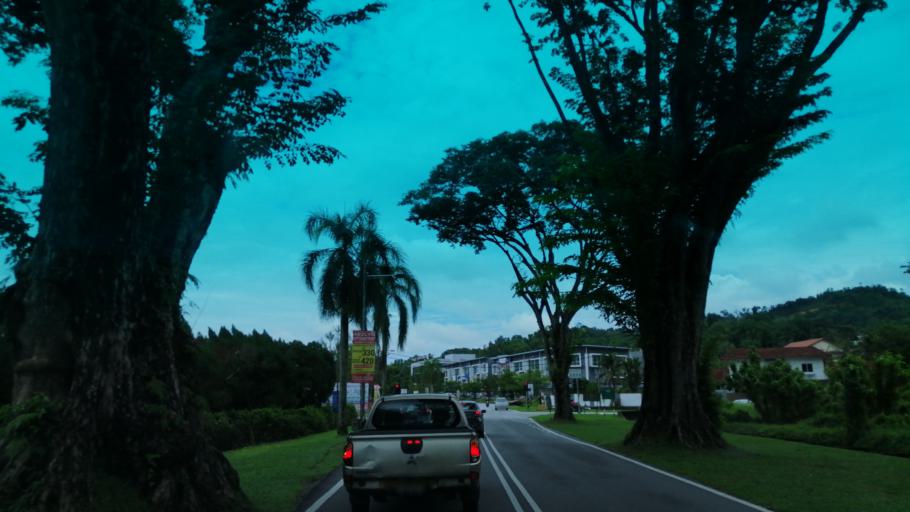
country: MY
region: Perak
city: Taiping
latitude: 4.8591
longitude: 100.7380
